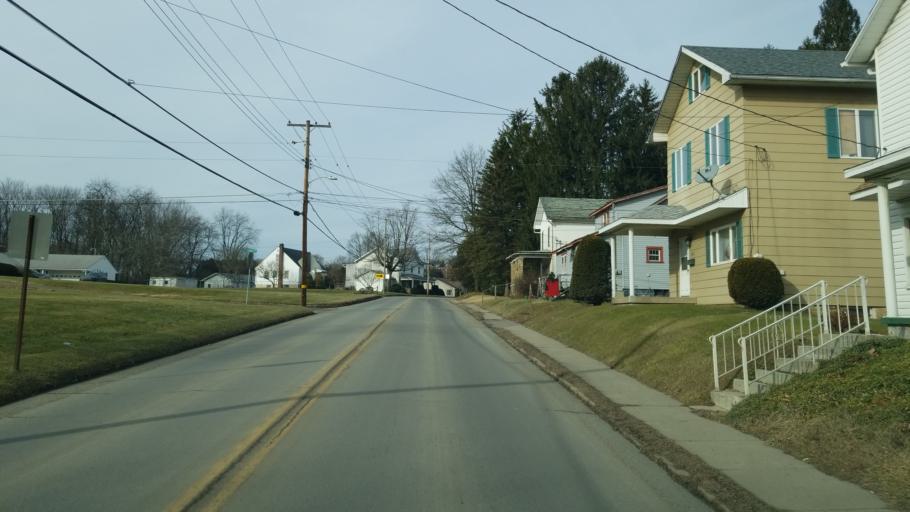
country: US
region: Pennsylvania
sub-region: Jefferson County
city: Punxsutawney
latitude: 40.9491
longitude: -78.9965
